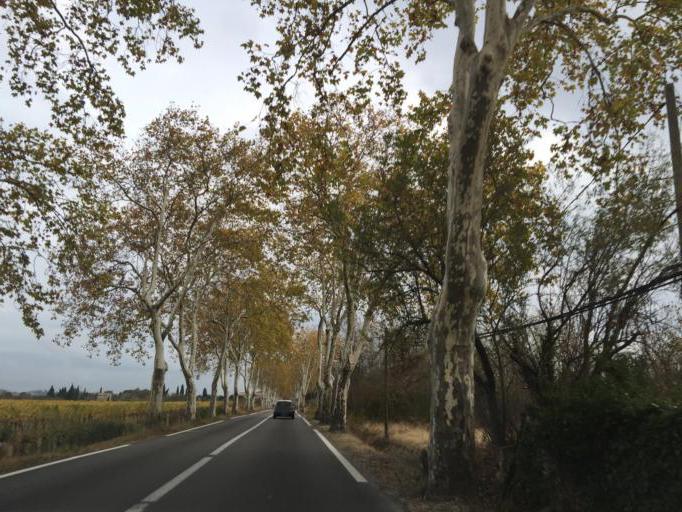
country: FR
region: Languedoc-Roussillon
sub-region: Departement du Gard
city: Remoulins
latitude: 43.9521
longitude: 4.5669
